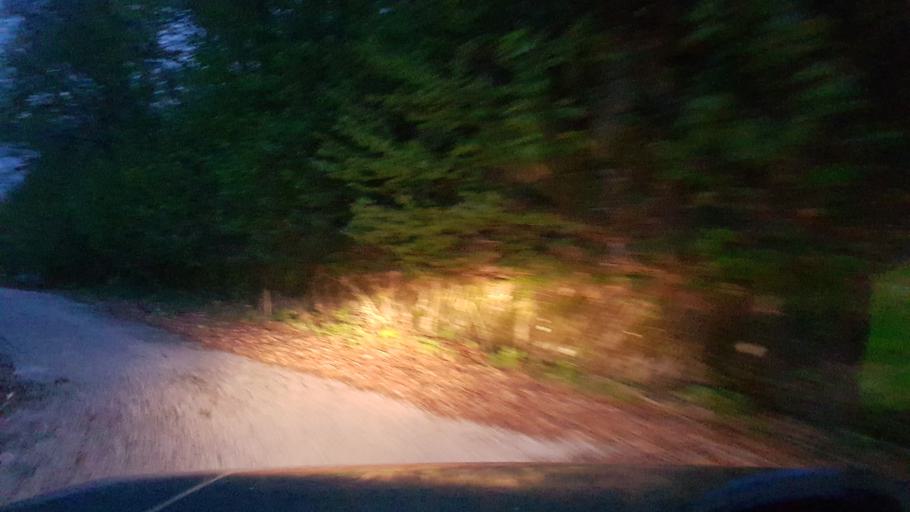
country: IT
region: Friuli Venezia Giulia
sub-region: Provincia di Udine
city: Taipana
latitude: 46.2403
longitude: 13.3540
